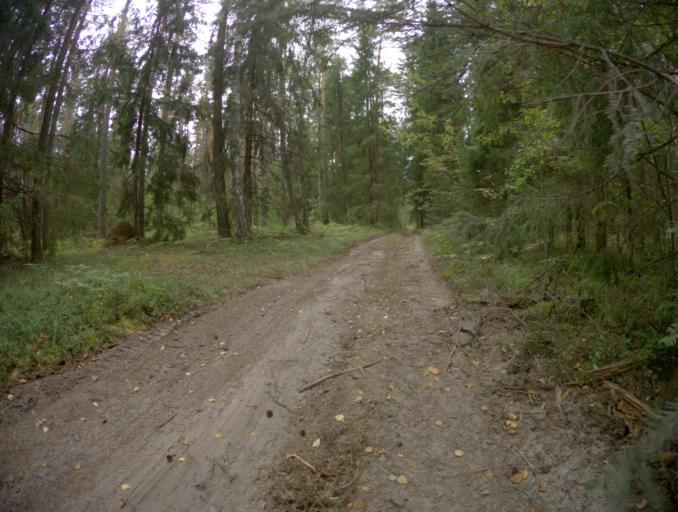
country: RU
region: Vladimir
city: Orgtrud
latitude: 56.1239
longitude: 40.7425
